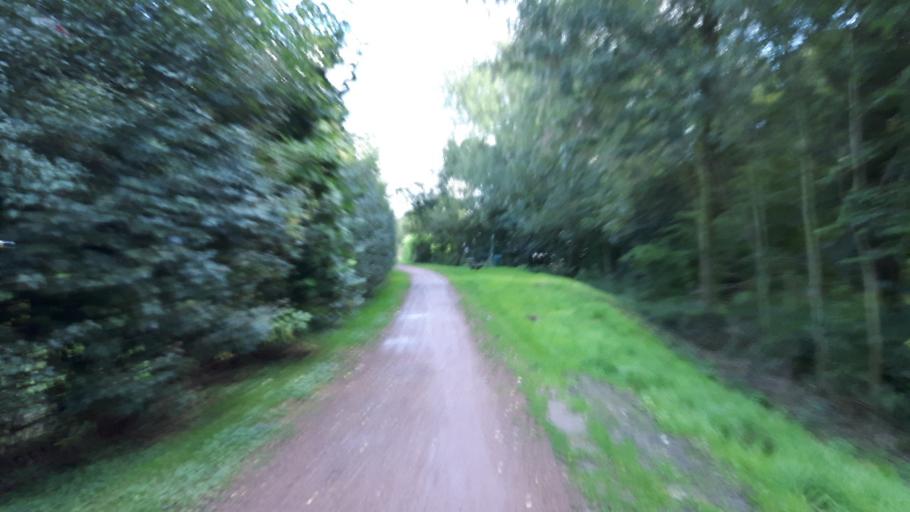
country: NL
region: South Holland
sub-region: Gemeente Leerdam
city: Leerdam
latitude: 51.8737
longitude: 5.0654
